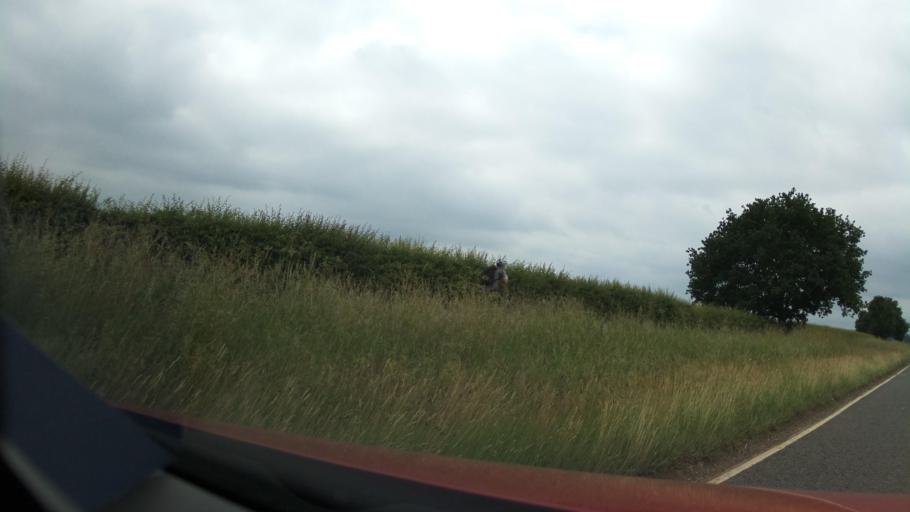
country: GB
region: England
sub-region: District of Rutland
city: Burley
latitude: 52.6719
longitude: -0.6977
